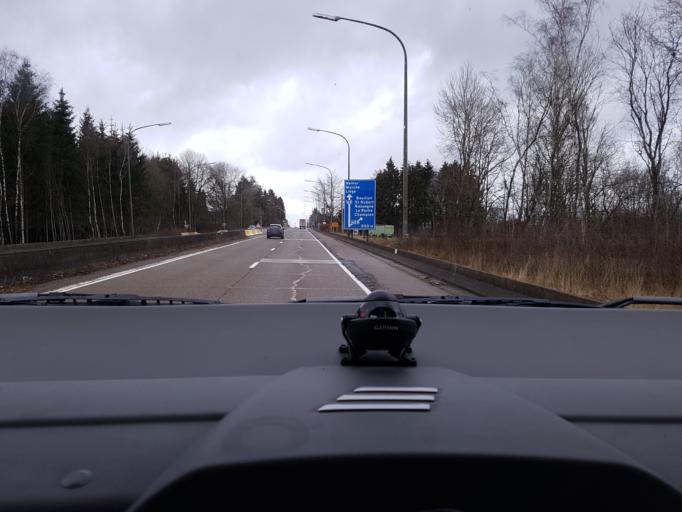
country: BE
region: Wallonia
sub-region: Province du Luxembourg
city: Tenneville
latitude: 50.1010
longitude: 5.4798
